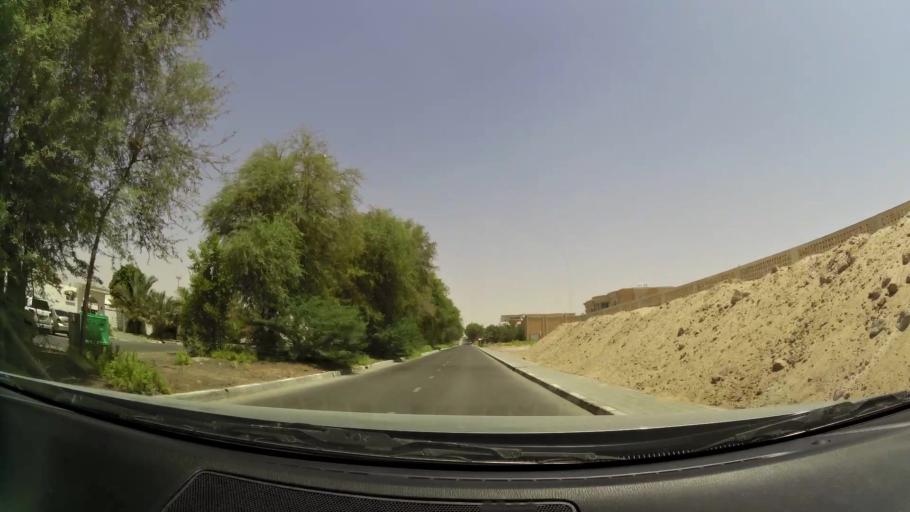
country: OM
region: Al Buraimi
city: Al Buraymi
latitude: 24.2731
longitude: 55.7485
